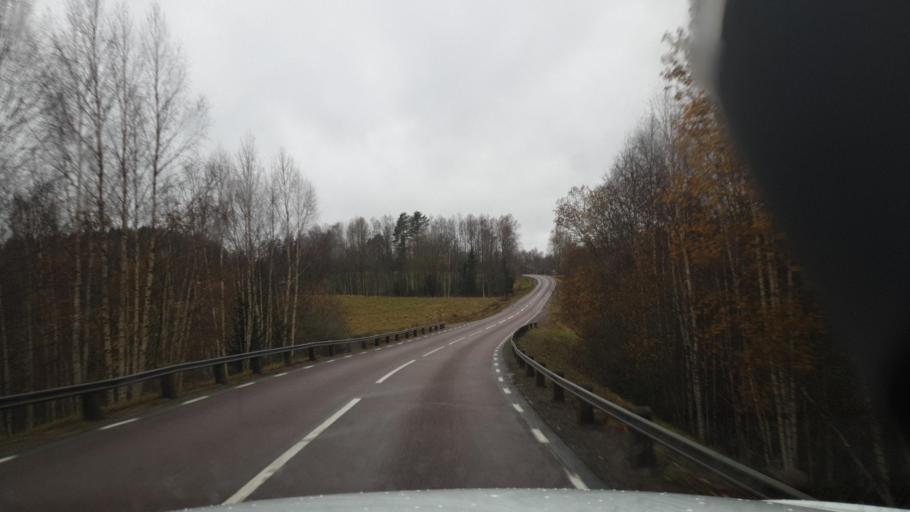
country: SE
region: Vaermland
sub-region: Sunne Kommun
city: Sunne
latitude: 59.6769
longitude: 13.0363
